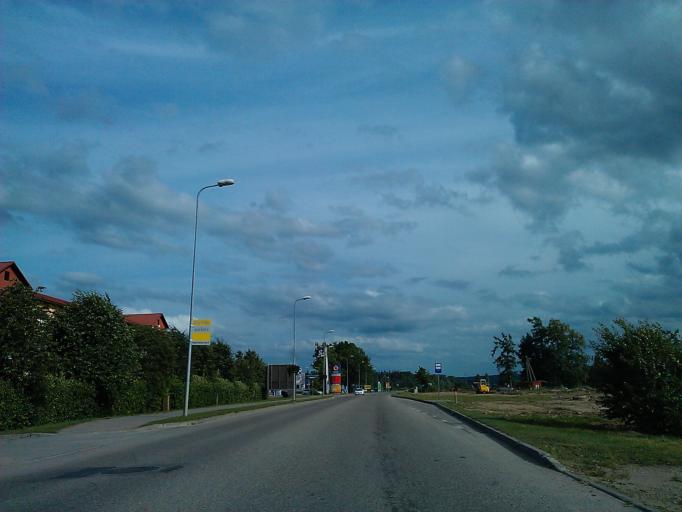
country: LV
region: Cesu Rajons
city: Cesis
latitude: 57.2996
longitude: 25.2983
